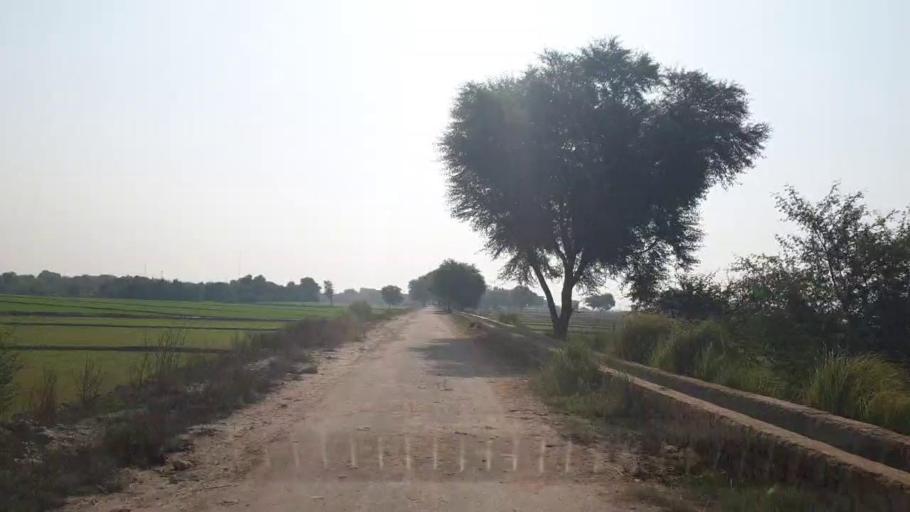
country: PK
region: Sindh
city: Sehwan
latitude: 26.4401
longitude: 67.8401
